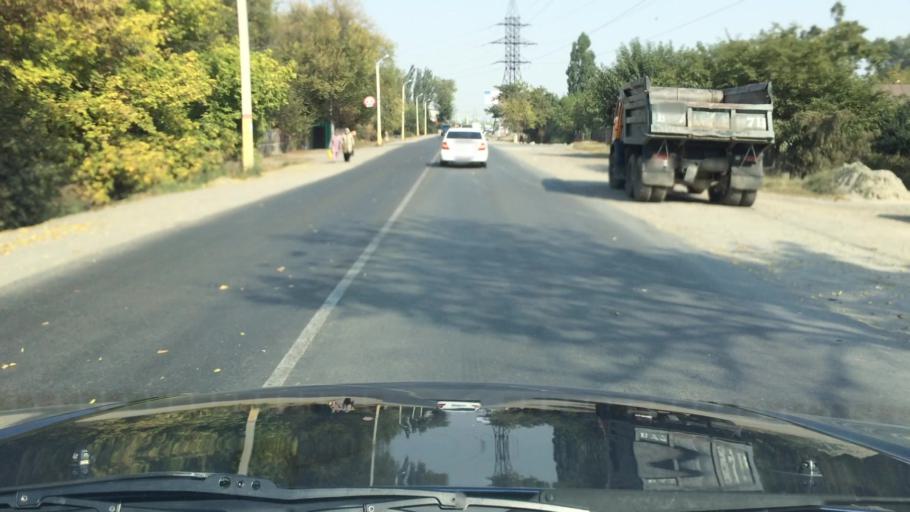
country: KG
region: Chuy
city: Lebedinovka
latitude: 42.8869
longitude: 74.6788
